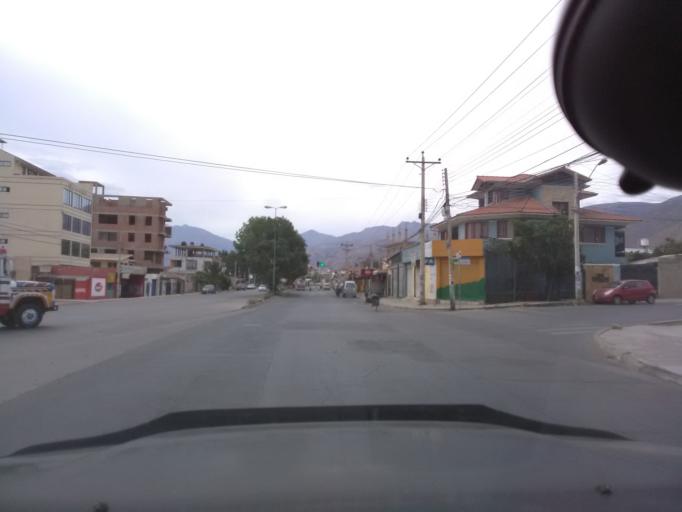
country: BO
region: Cochabamba
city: Cochabamba
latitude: -17.3563
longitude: -66.1774
